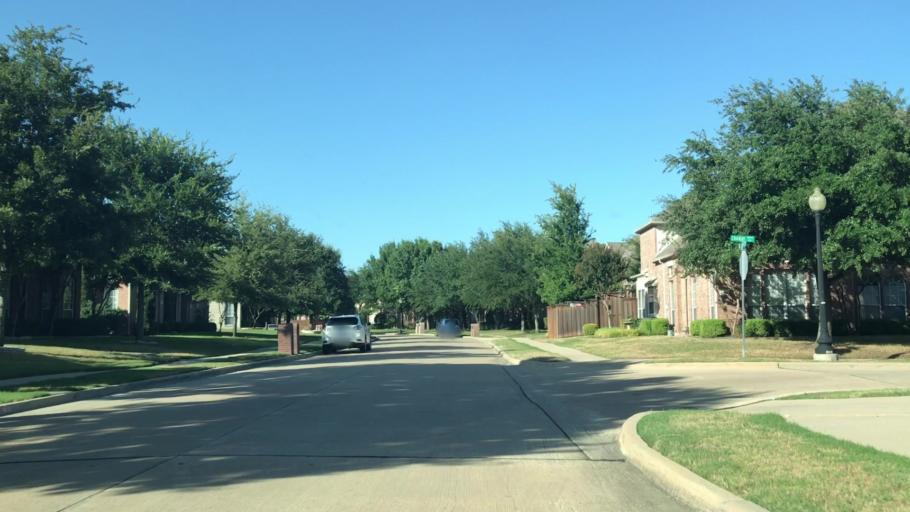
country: US
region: Texas
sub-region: Collin County
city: Frisco
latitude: 33.1345
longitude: -96.7841
